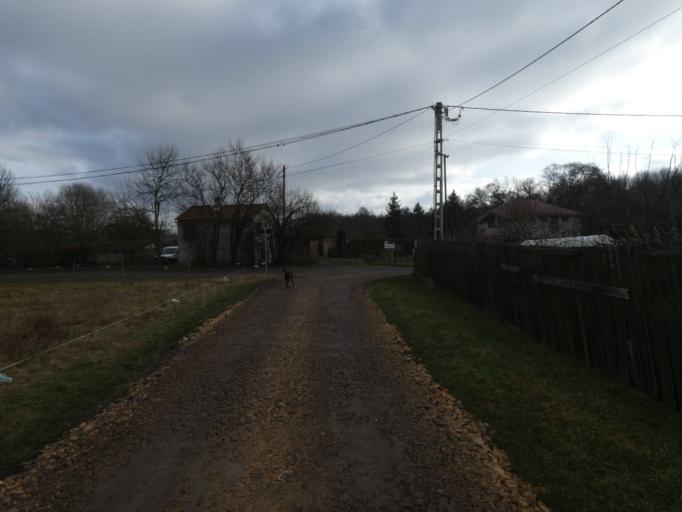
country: HU
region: Budapest
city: Budapest XVI. keruelet
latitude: 47.4917
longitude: 19.2009
